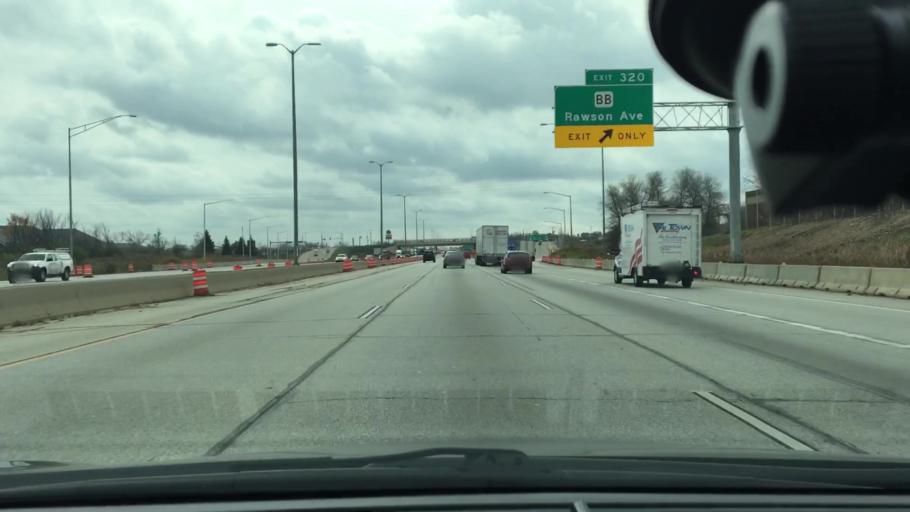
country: US
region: Wisconsin
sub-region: Milwaukee County
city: Greendale
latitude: 42.9218
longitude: -87.9356
